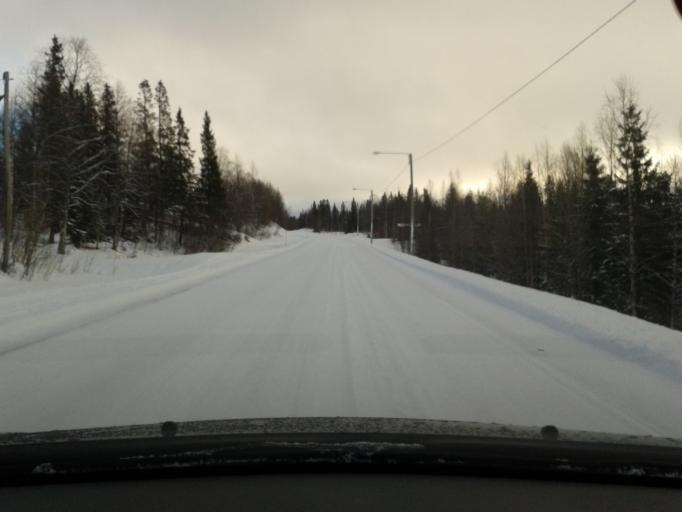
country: SE
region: Vaesterbotten
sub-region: Vilhelmina Kommun
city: Sjoberg
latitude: 65.2507
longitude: 15.5845
